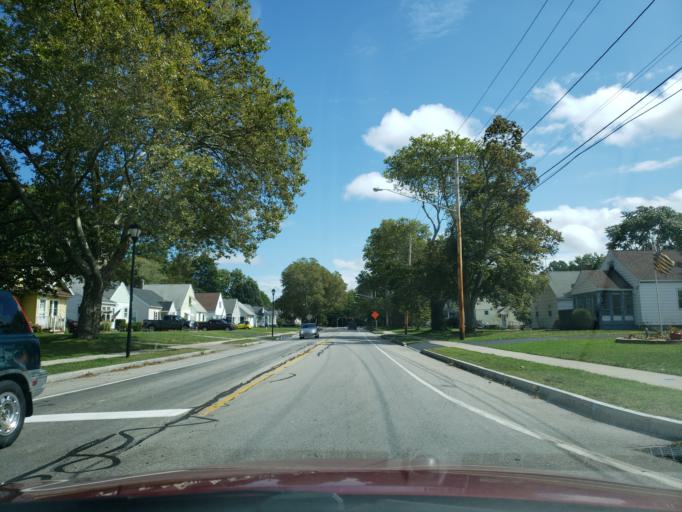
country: US
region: New York
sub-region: Monroe County
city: Greece
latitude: 43.2311
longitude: -77.6508
